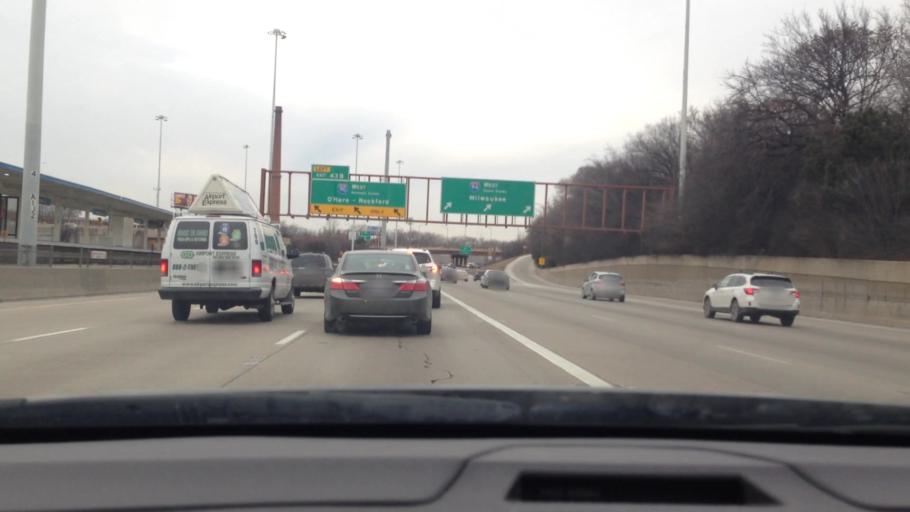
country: US
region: Illinois
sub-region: Cook County
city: Lincolnwood
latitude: 41.9616
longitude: -87.7431
